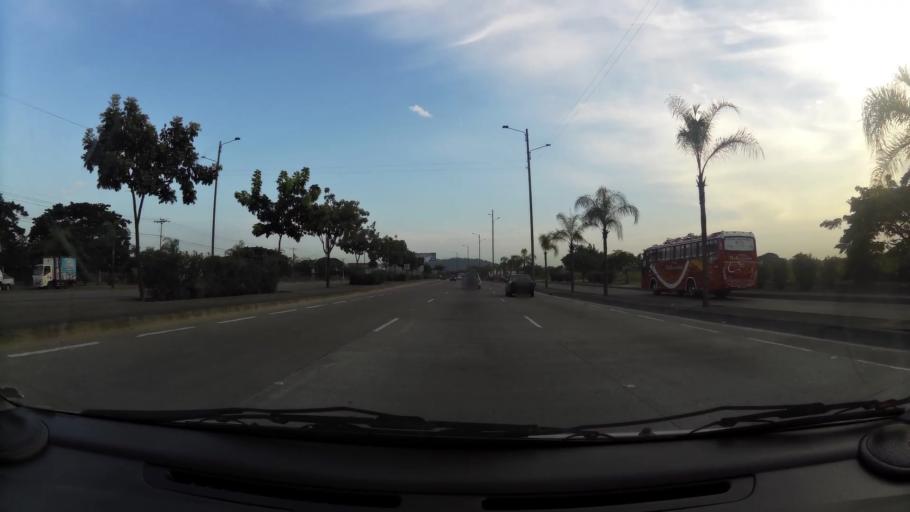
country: EC
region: Guayas
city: Eloy Alfaro
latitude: -2.0927
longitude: -79.8938
